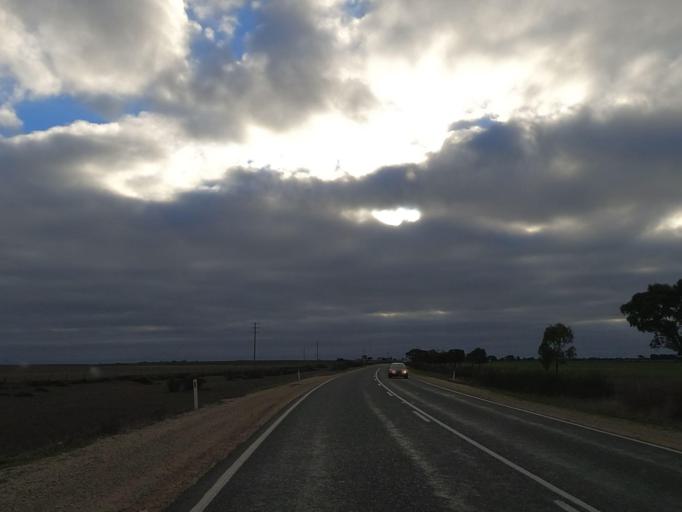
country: AU
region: Victoria
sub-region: Swan Hill
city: Swan Hill
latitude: -35.6495
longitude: 143.8394
